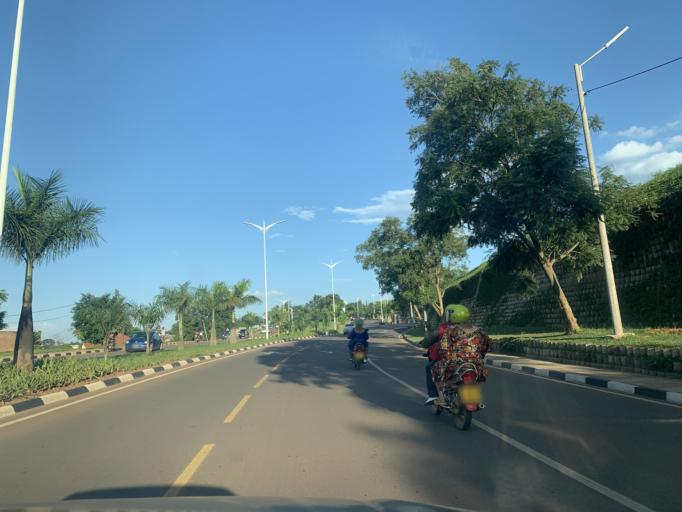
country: RW
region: Kigali
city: Kigali
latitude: -1.9637
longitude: 30.1286
